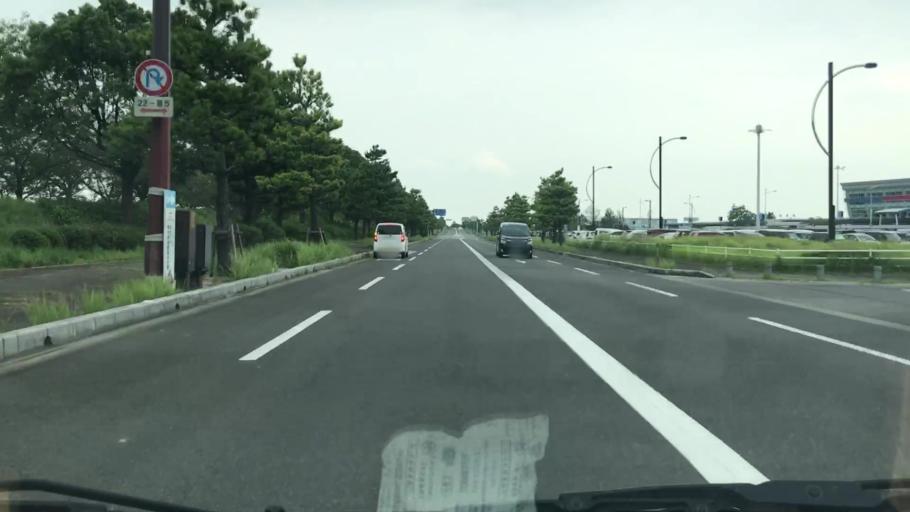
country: JP
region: Saga Prefecture
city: Okawa
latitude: 33.1552
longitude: 130.3020
